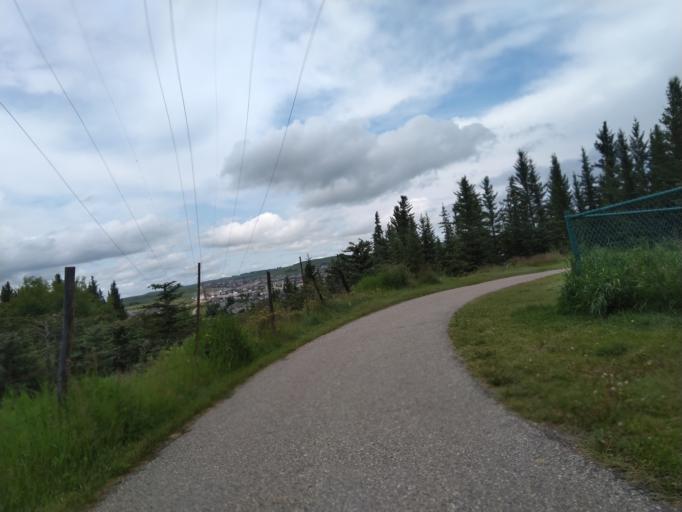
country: CA
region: Alberta
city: Cochrane
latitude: 51.1899
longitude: -114.5132
